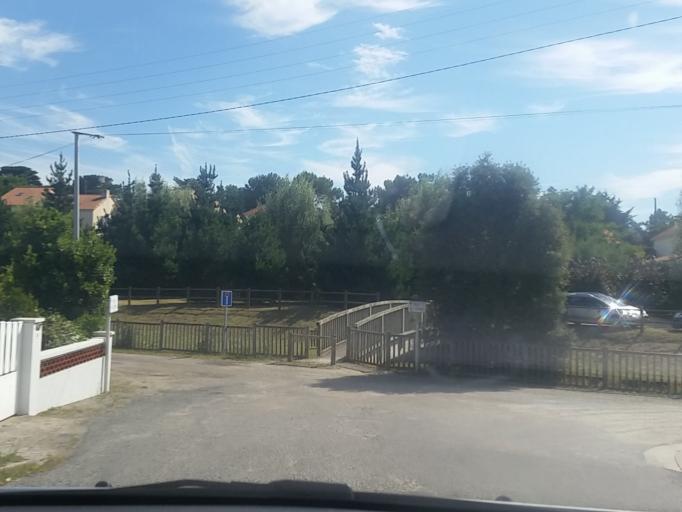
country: FR
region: Pays de la Loire
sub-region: Departement de la Loire-Atlantique
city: Saint-Michel-Chef-Chef
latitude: 47.1719
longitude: -2.1633
